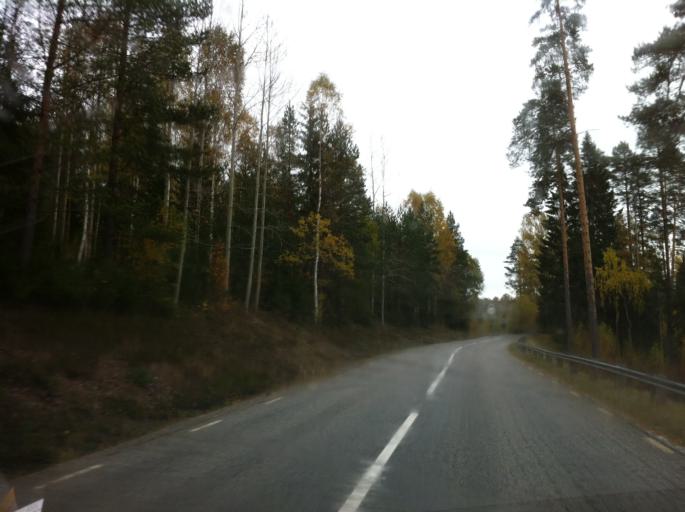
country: SE
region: OErebro
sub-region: Lindesbergs Kommun
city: Stora
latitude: 59.6592
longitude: 15.0792
